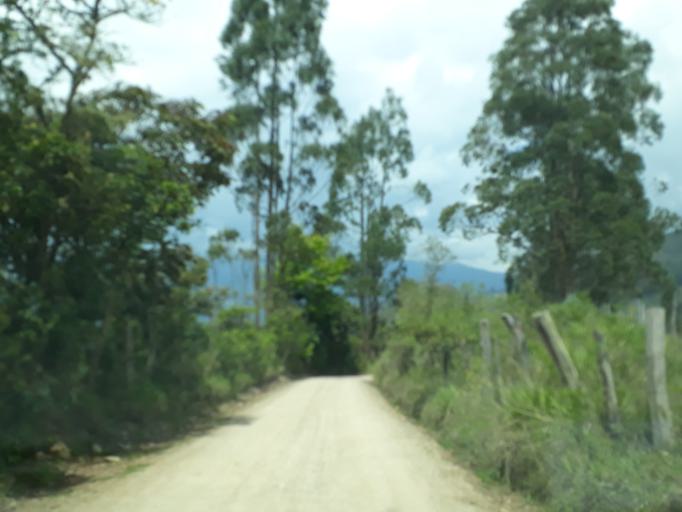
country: CO
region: Cundinamarca
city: Macheta
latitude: 5.0934
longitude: -73.5617
